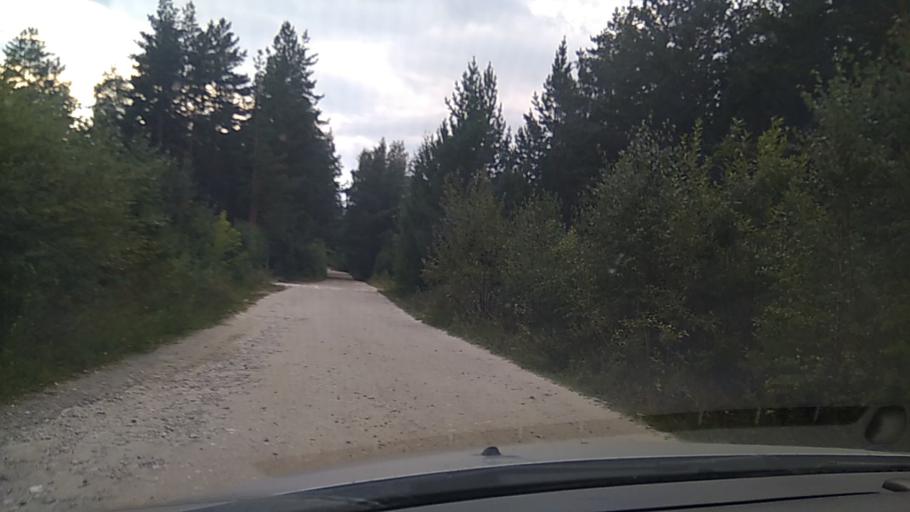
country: RU
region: Chelyabinsk
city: Kyshtym
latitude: 55.6797
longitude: 60.5786
